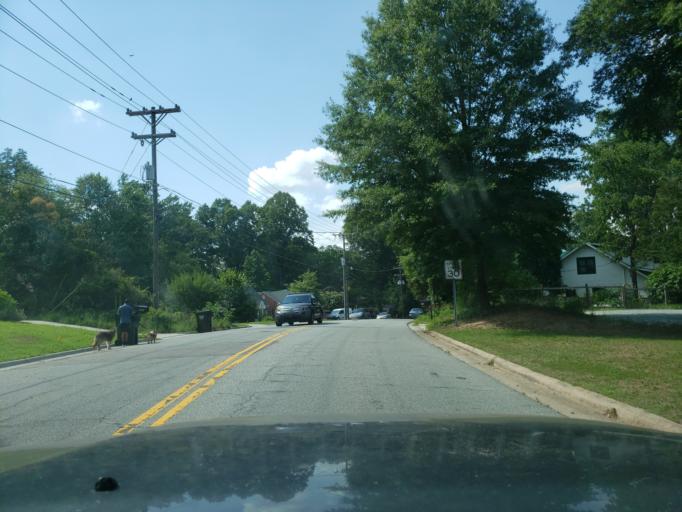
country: US
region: North Carolina
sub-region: Durham County
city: Durham
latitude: 35.9748
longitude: -78.9169
